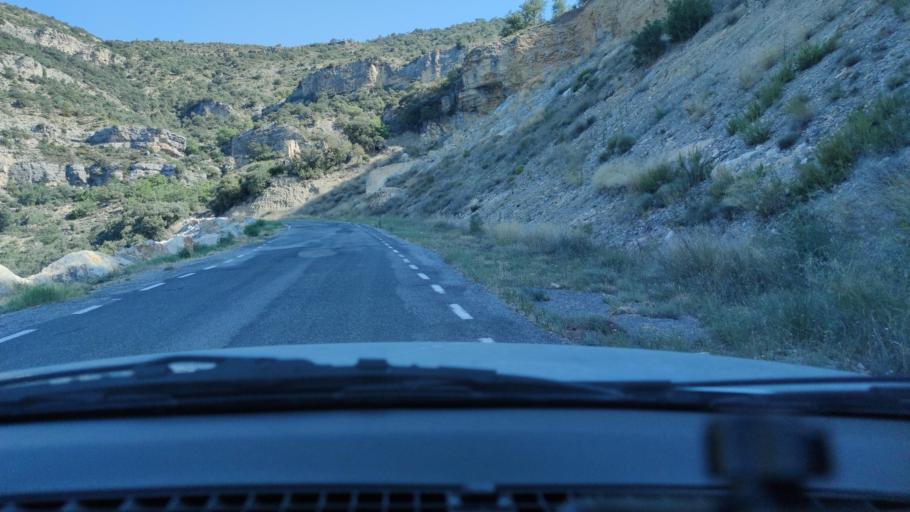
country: ES
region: Catalonia
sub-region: Provincia de Lleida
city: Llimiana
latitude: 42.0838
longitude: 0.8560
